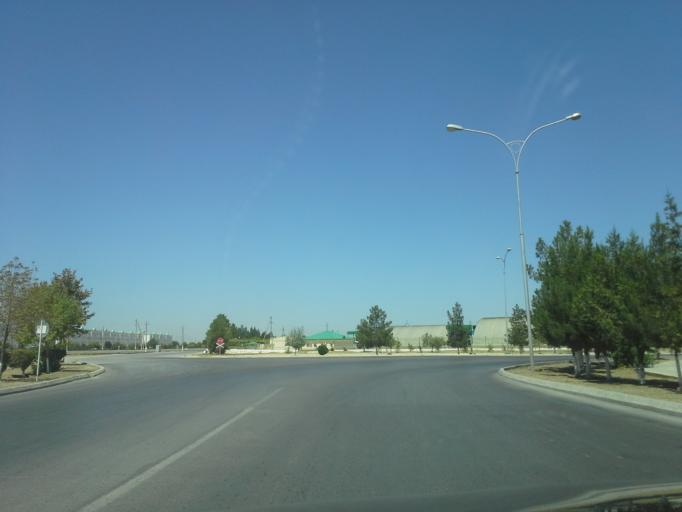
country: TM
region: Ahal
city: Ashgabat
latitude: 37.9913
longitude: 58.3216
